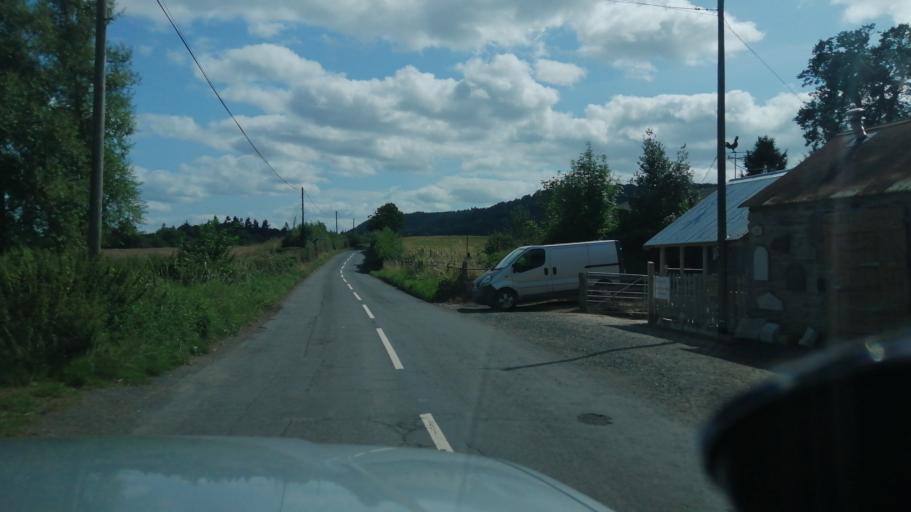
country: GB
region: England
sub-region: Herefordshire
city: Moccas
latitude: 52.0942
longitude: -2.9762
